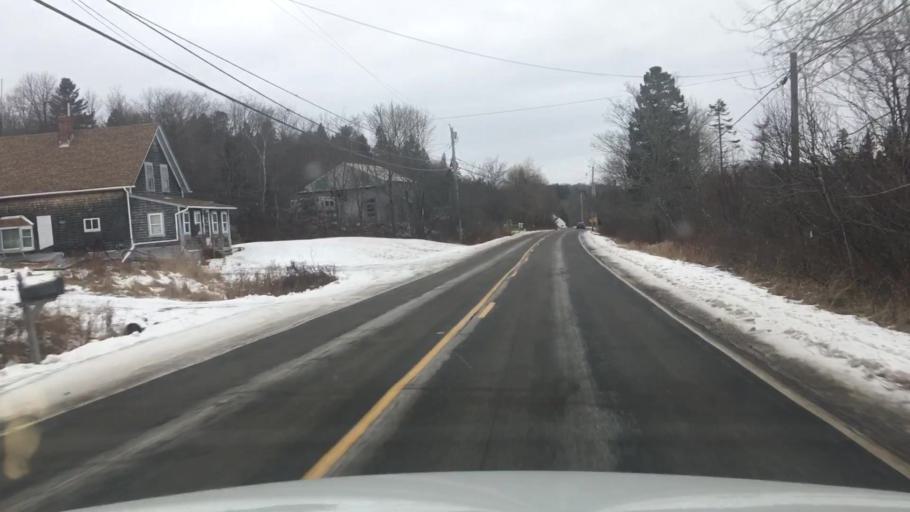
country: US
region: Maine
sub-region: Washington County
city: East Machias
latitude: 44.7275
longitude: -67.3886
